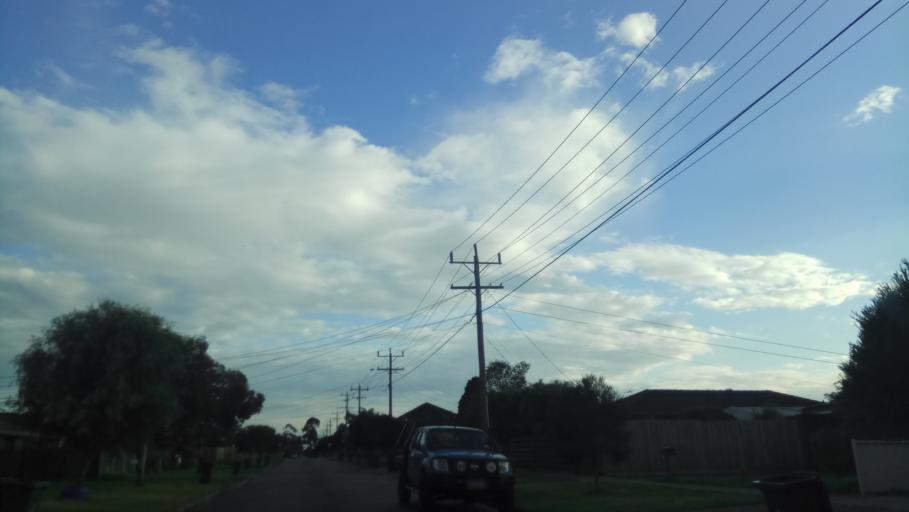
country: AU
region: Victoria
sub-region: Hobsons Bay
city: Laverton
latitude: -37.8698
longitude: 144.7766
